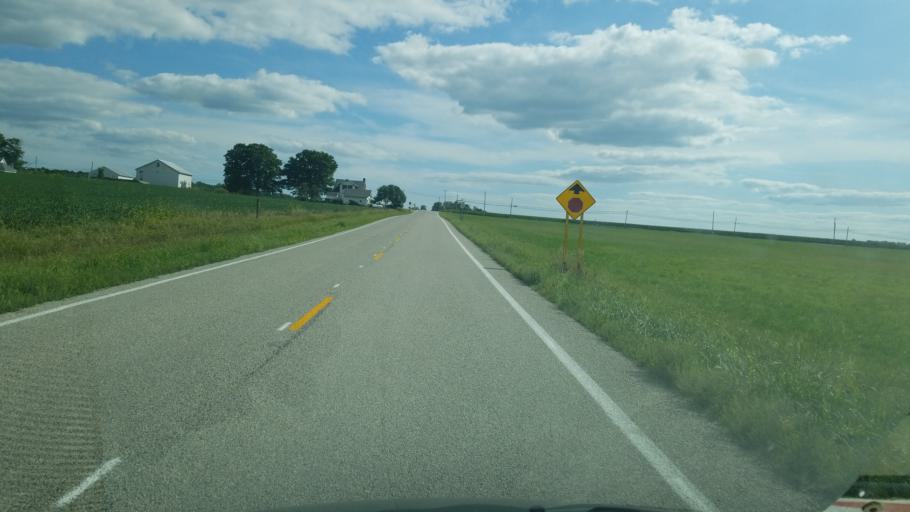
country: US
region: Ohio
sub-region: Champaign County
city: Saint Paris
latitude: 40.2202
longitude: -83.9410
